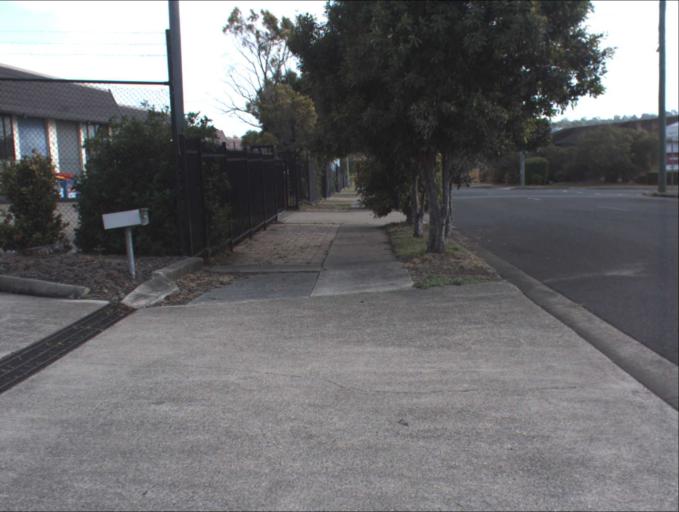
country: AU
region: Queensland
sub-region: Logan
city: Springwood
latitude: -27.6182
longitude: 153.1185
